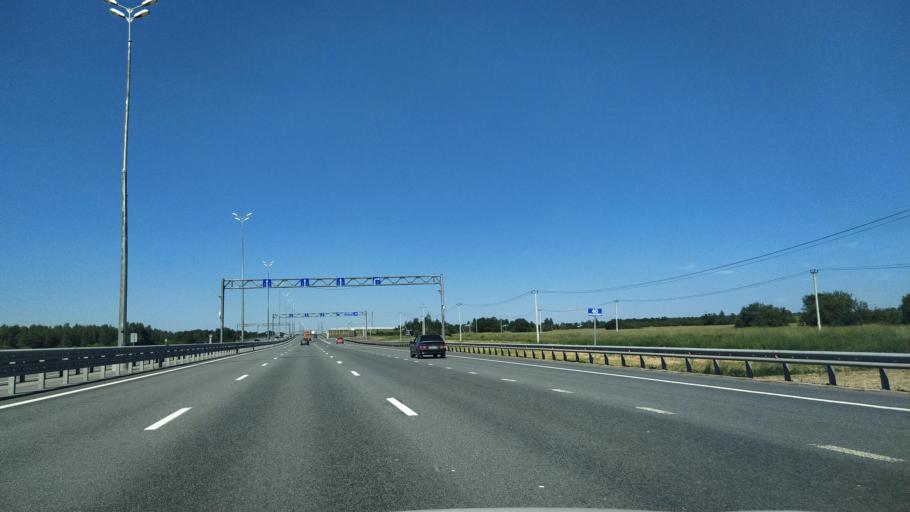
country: RU
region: Leningrad
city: Maloye Verevo
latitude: 59.6016
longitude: 30.1820
